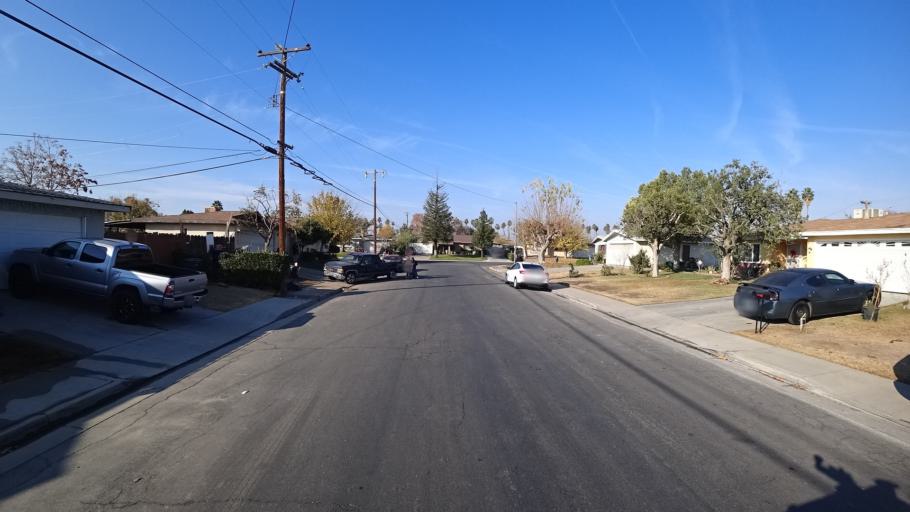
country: US
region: California
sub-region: Kern County
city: Greenfield
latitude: 35.3160
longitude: -119.0150
